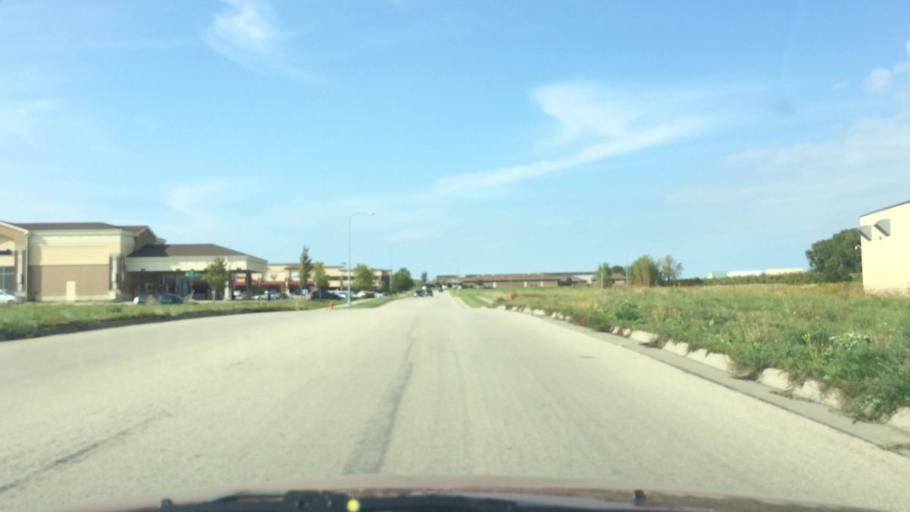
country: US
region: Minnesota
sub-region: Olmsted County
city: Rochester
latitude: 44.0504
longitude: -92.5203
